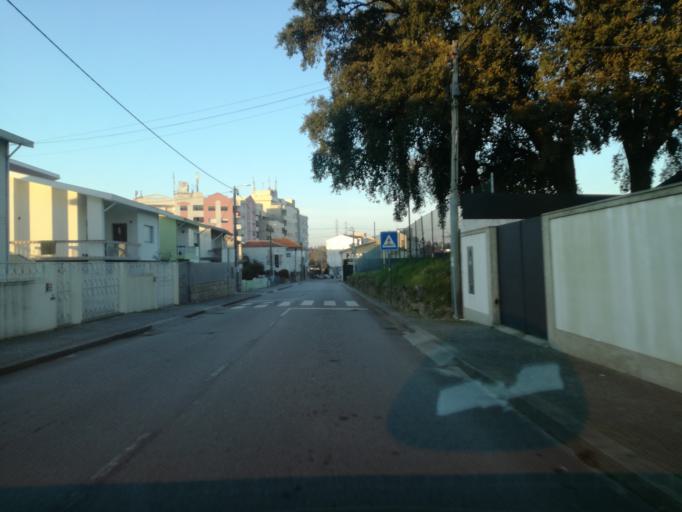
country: PT
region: Porto
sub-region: Maia
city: Milheiros
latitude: 41.2279
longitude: -8.5887
